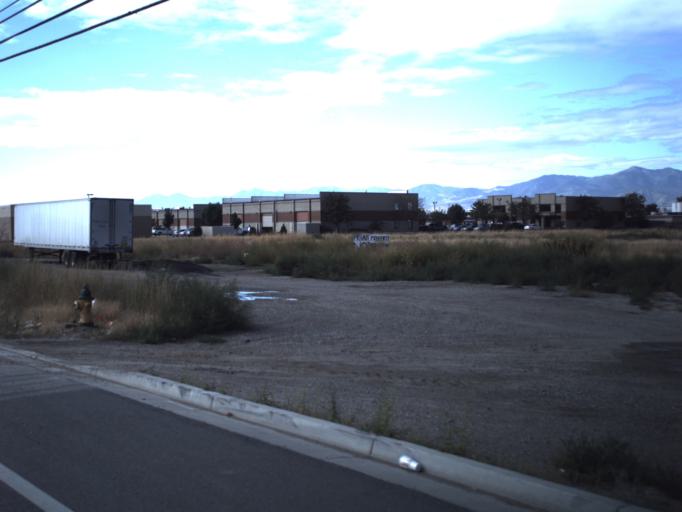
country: US
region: Utah
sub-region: Salt Lake County
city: Salt Lake City
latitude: 40.7453
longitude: -111.9391
